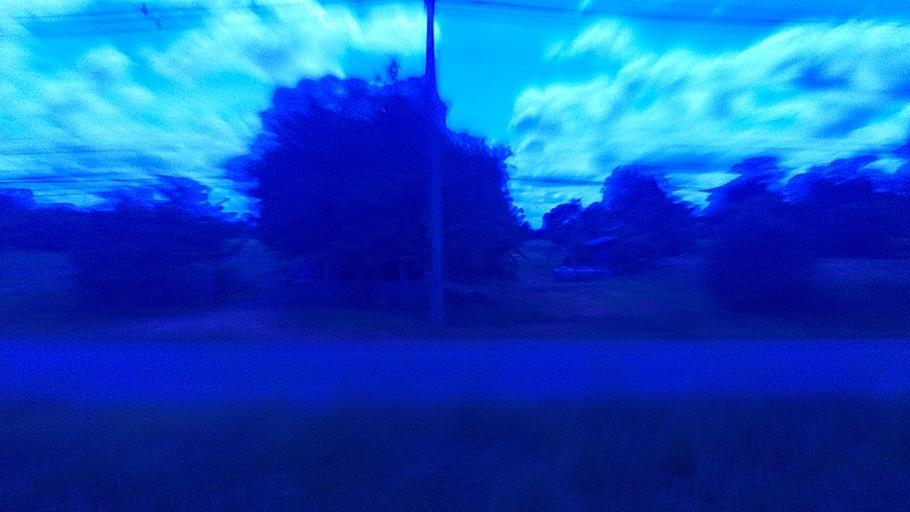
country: TH
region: Nakhon Ratchasima
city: Dan Khun Thot
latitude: 15.1047
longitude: 101.7216
